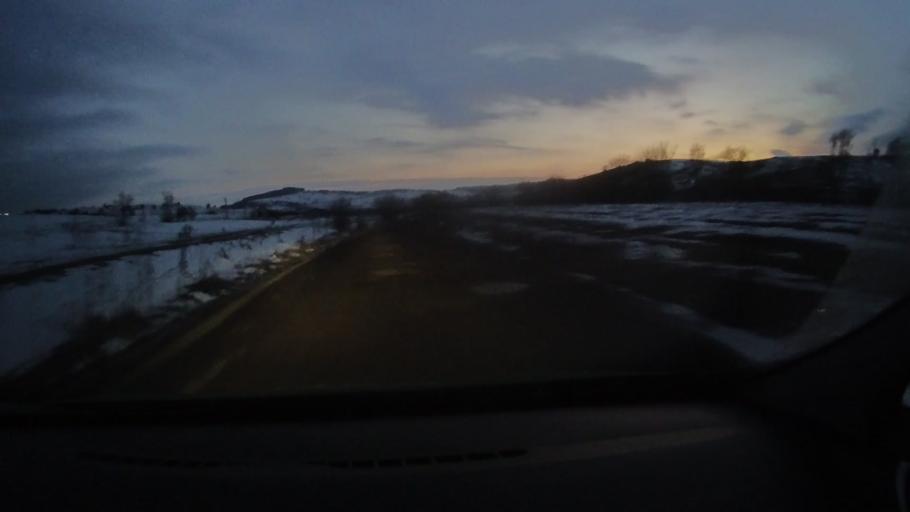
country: RO
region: Harghita
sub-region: Comuna Darjiu
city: Darjiu
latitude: 46.1577
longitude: 25.2039
